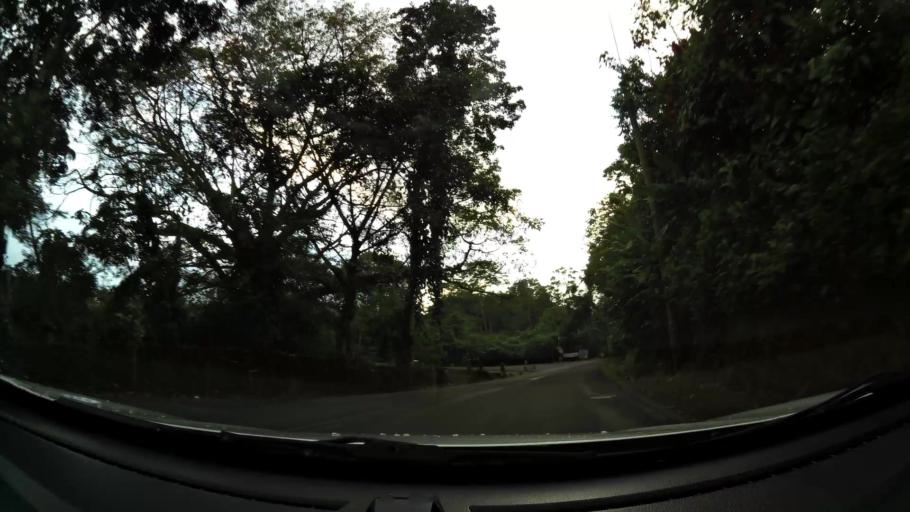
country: CR
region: Cartago
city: Turrialba
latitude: 9.9015
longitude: -83.6873
